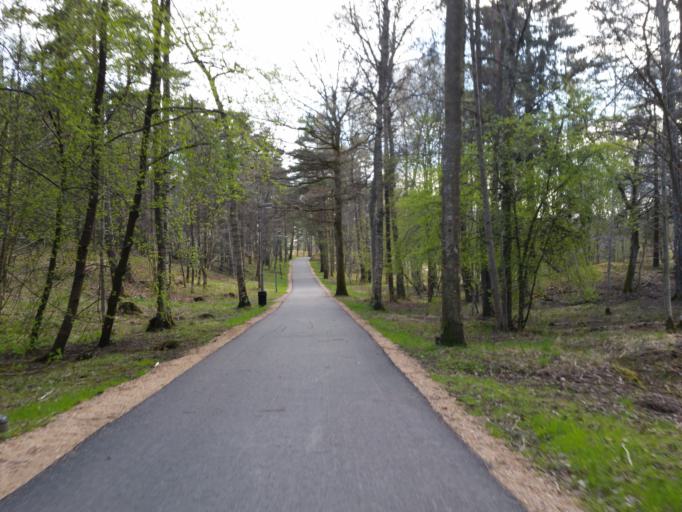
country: SE
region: Vaestra Goetaland
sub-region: Trollhattan
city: Trollhattan
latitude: 58.2788
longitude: 12.2919
